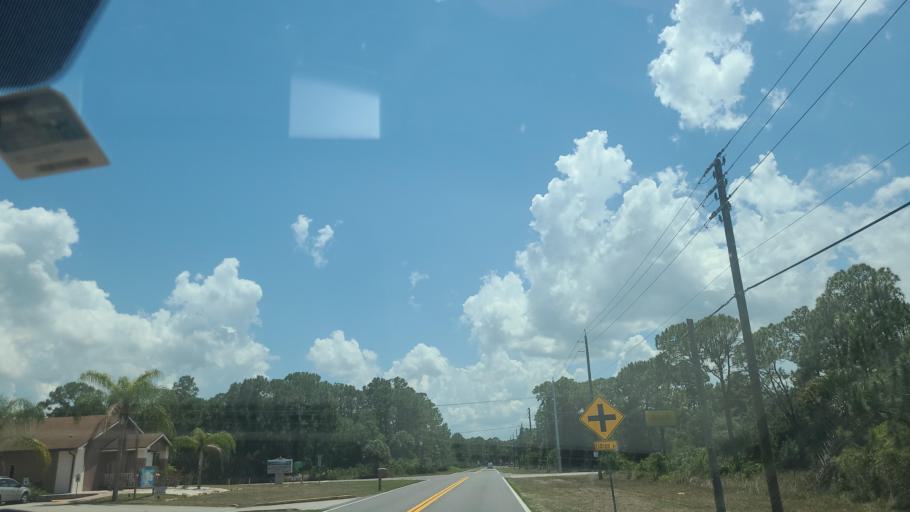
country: US
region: Florida
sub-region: Brevard County
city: Grant-Valkaria
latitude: 27.9336
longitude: -80.6352
